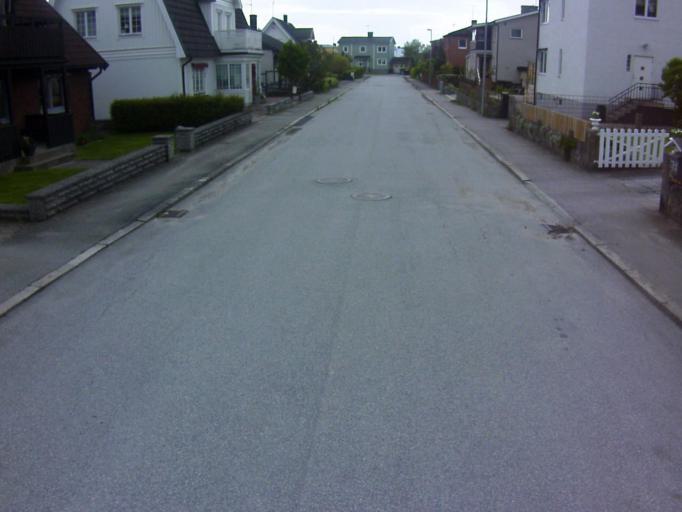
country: SE
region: Blekinge
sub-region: Solvesborgs Kommun
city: Soelvesborg
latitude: 56.0521
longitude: 14.5733
